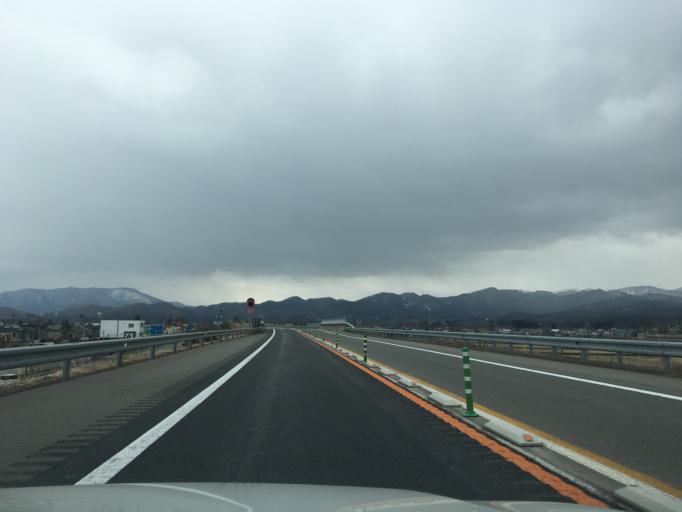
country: JP
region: Aomori
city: Aomori Shi
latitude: 40.7956
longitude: 140.7711
